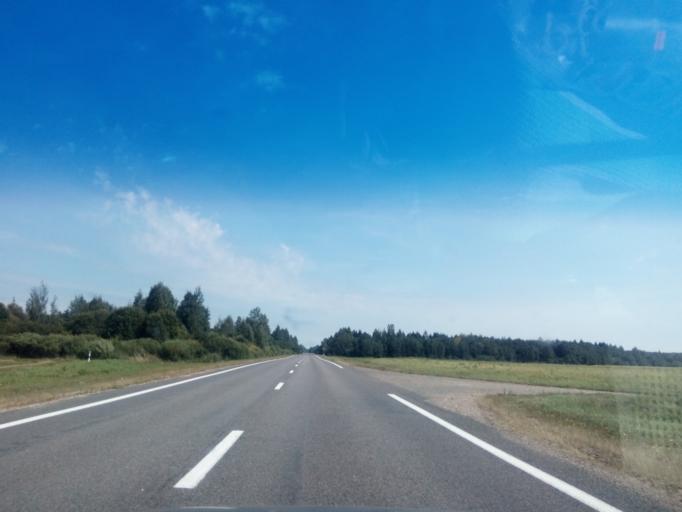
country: BY
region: Vitebsk
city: Vyerkhnyadzvinsk
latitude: 55.8255
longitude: 27.7881
